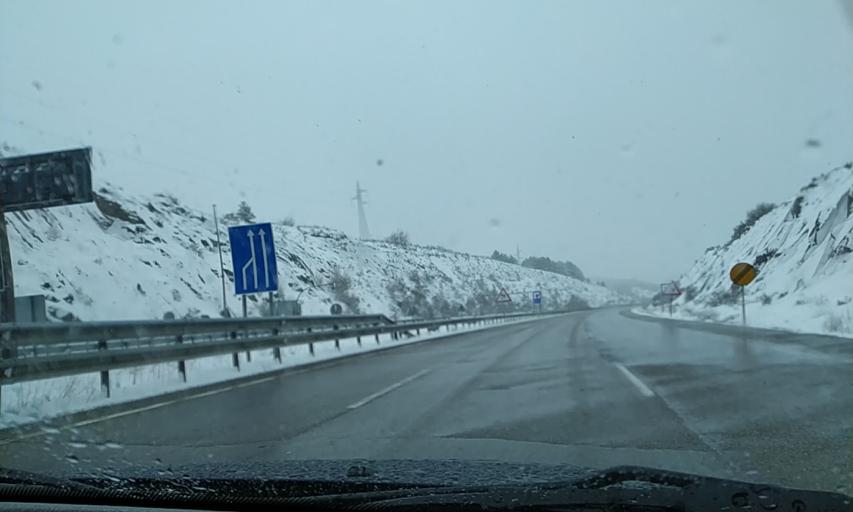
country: ES
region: Castille and Leon
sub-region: Provincia de Zamora
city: Requejo
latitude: 42.0396
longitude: -6.8084
